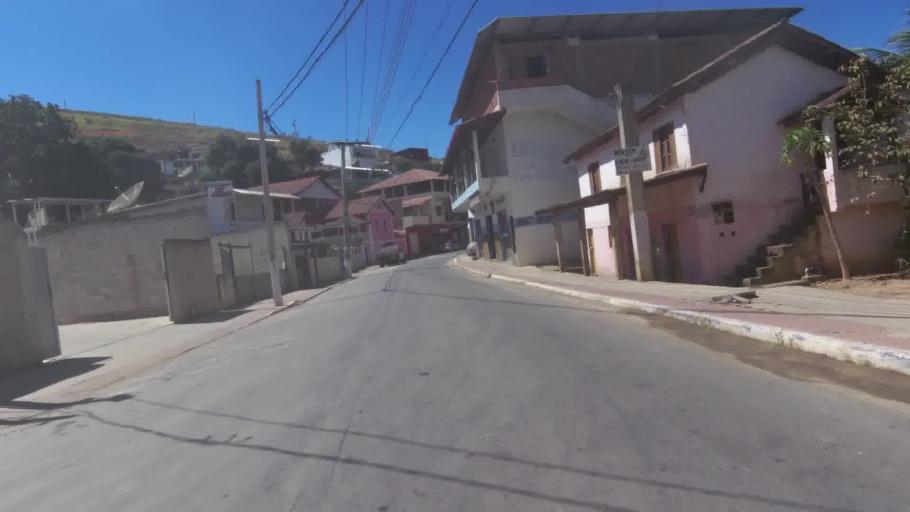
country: BR
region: Espirito Santo
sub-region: Cachoeiro De Itapemirim
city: Cachoeiro de Itapemirim
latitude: -20.9142
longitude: -41.1946
